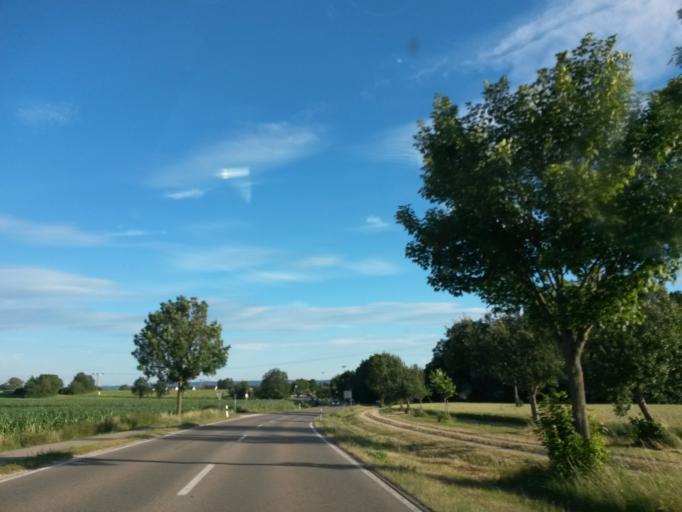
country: DE
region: Baden-Wuerttemberg
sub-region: Regierungsbezirk Stuttgart
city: Ellwangen
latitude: 48.9657
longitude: 10.1638
